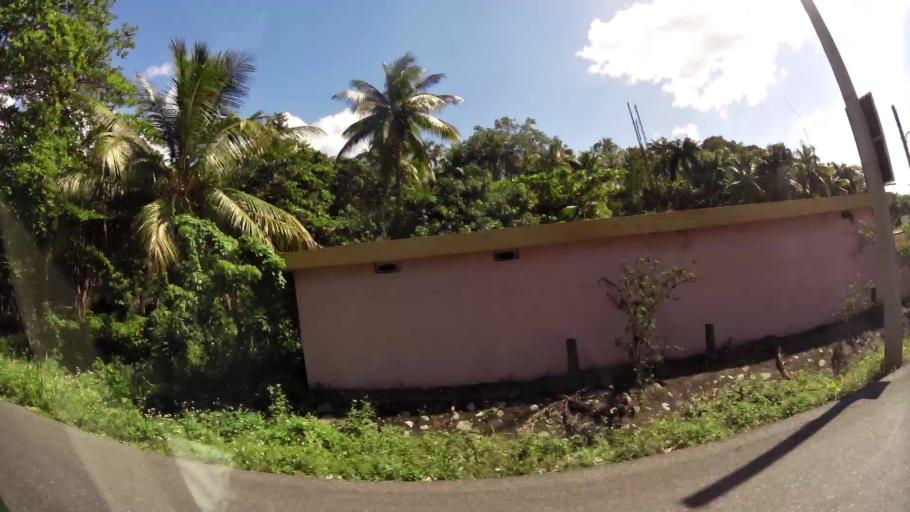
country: DO
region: San Cristobal
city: San Cristobal
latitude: 18.4294
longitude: -70.0893
